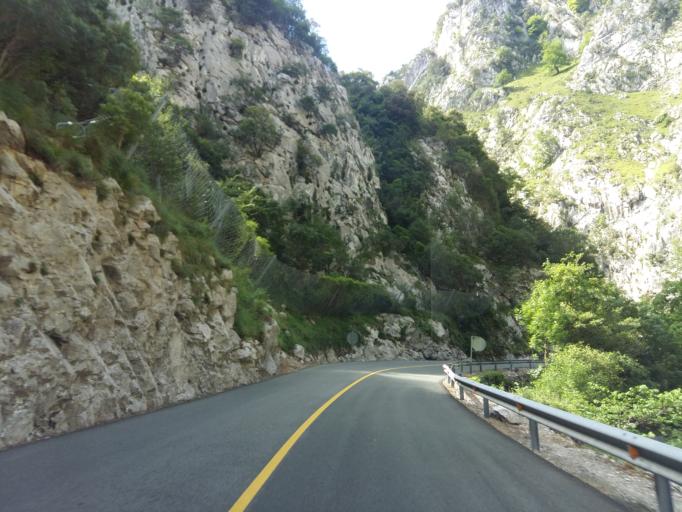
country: ES
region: Cantabria
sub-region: Provincia de Cantabria
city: Tresviso
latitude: 43.2416
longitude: -4.5822
